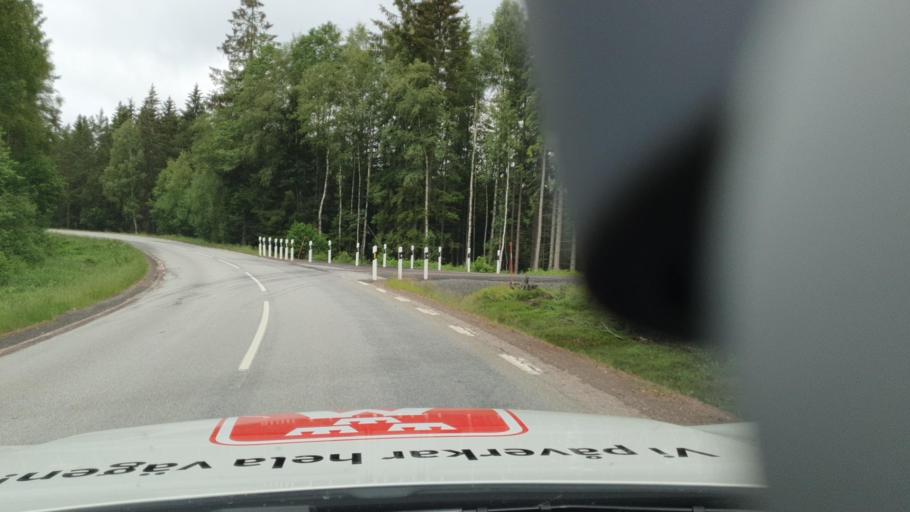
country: SE
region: Vaermland
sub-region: Kristinehamns Kommun
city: Bjorneborg
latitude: 59.1168
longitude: 14.2133
